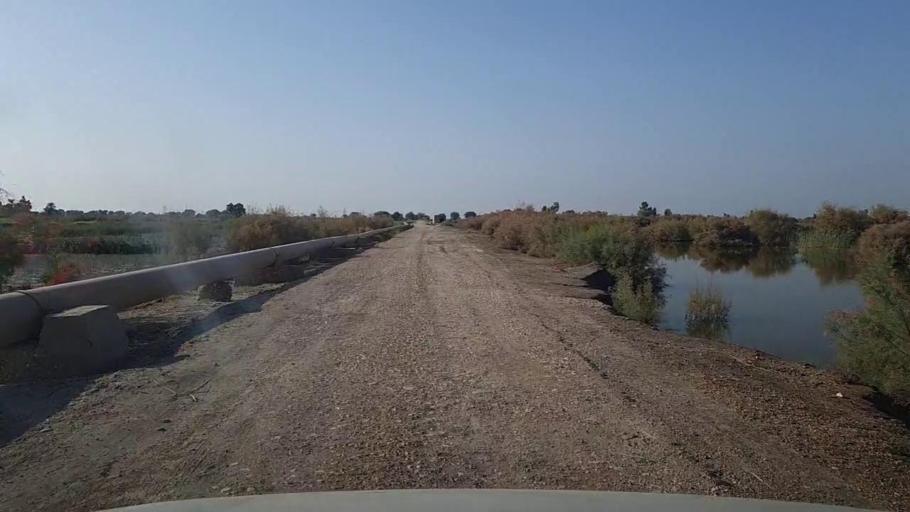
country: PK
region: Sindh
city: Kandhkot
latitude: 28.2835
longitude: 69.3349
